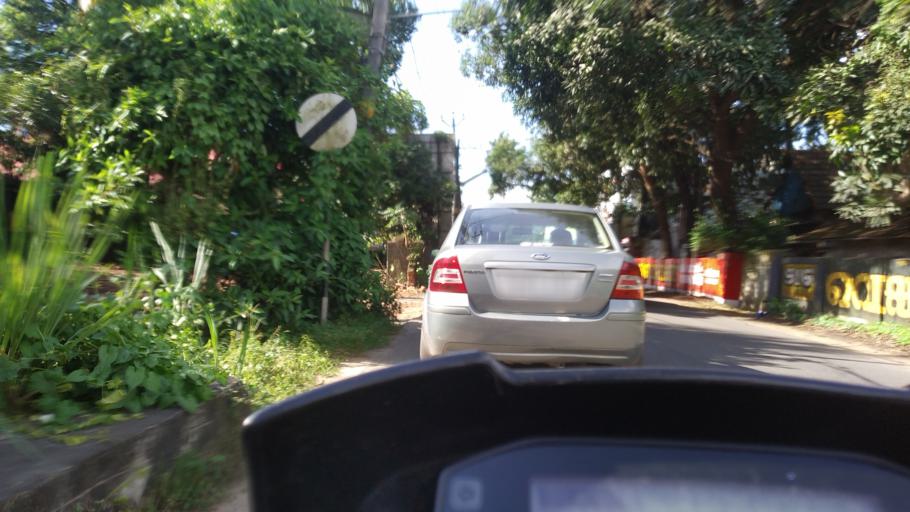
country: IN
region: Kerala
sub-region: Ernakulam
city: Elur
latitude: 10.0515
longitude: 76.2159
